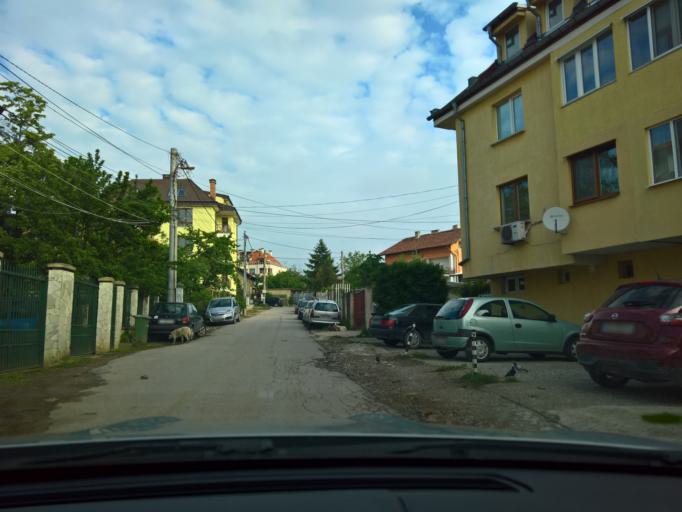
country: BG
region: Sofia-Capital
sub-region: Stolichna Obshtina
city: Sofia
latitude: 42.6689
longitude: 23.2476
